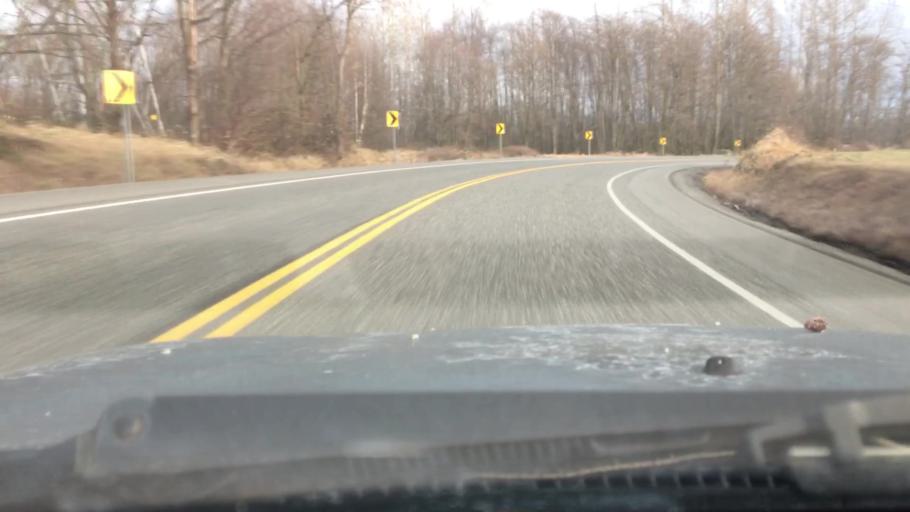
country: US
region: Washington
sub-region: Whatcom County
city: Birch Bay
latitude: 48.8628
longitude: -122.7026
